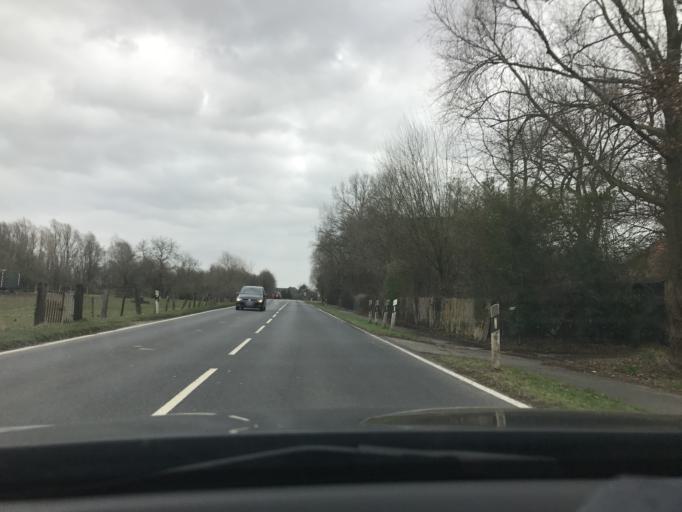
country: DE
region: North Rhine-Westphalia
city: Kempen
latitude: 51.3722
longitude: 6.4664
